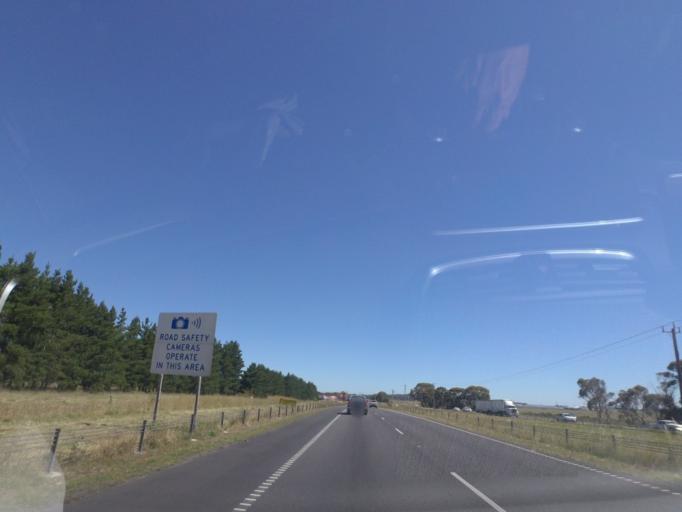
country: AU
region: Victoria
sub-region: Hume
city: Craigieburn
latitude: -37.5219
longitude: 144.9487
